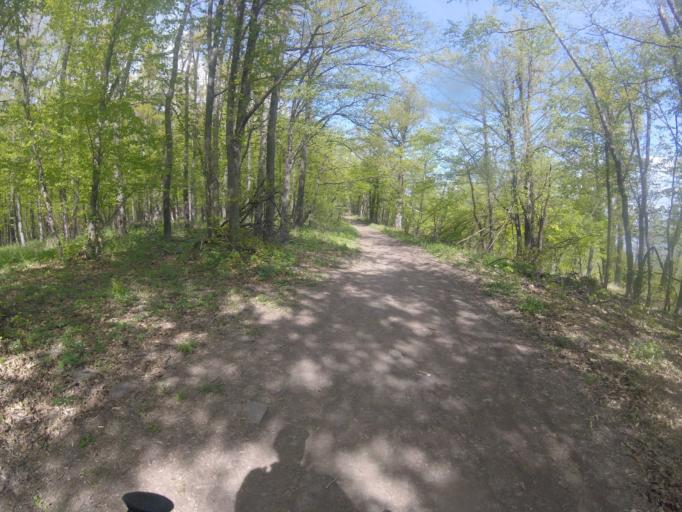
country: HU
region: Pest
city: Pilisszentkereszt
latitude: 47.7343
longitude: 18.9289
